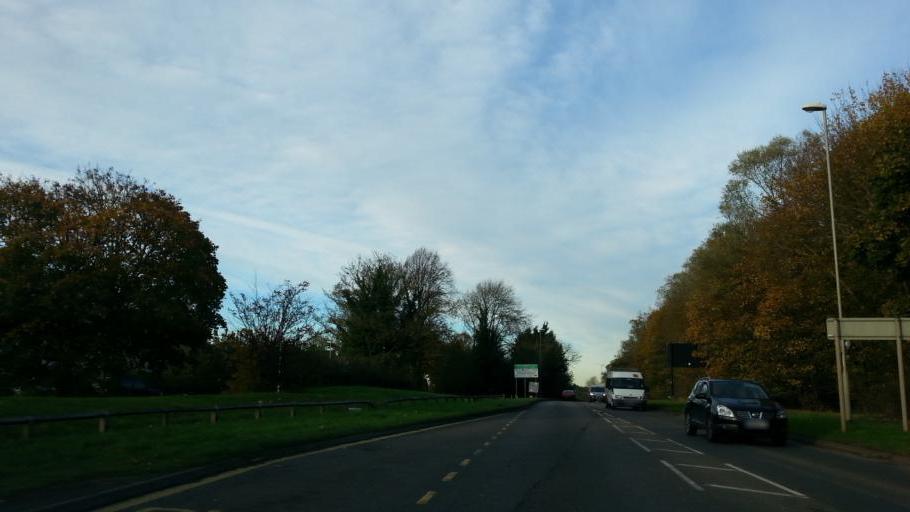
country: GB
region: England
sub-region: Northamptonshire
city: Northampton
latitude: 52.2791
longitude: -0.8452
